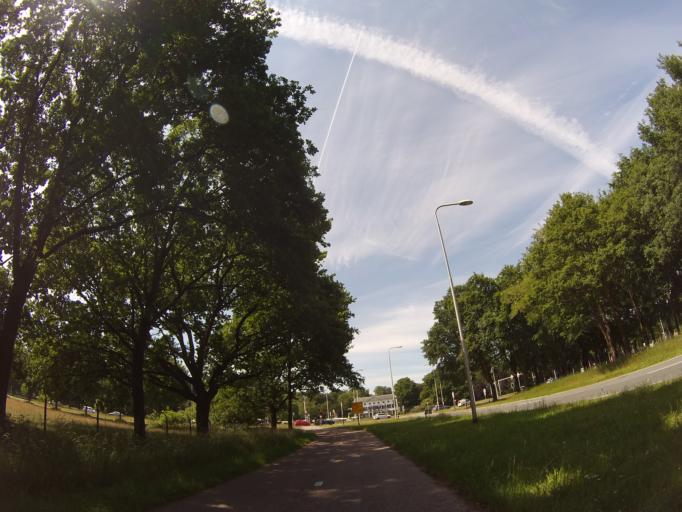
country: NL
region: Utrecht
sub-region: Gemeente De Bilt
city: De Bilt
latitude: 52.1017
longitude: 5.2066
